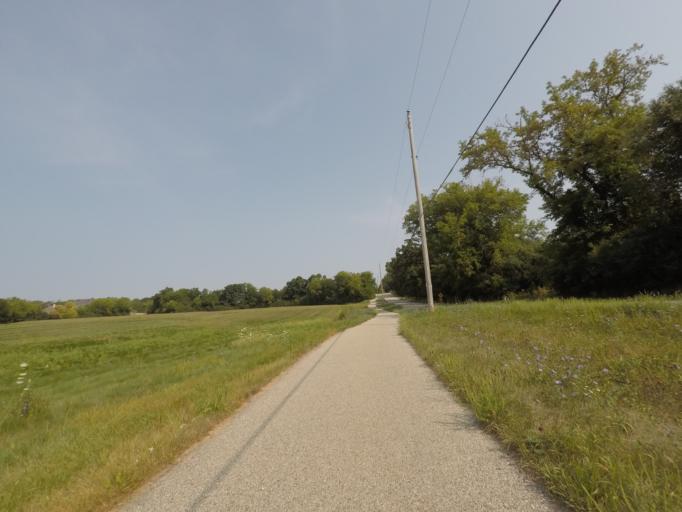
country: US
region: Wisconsin
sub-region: Waukesha County
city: Wales
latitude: 43.0206
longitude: -88.4139
